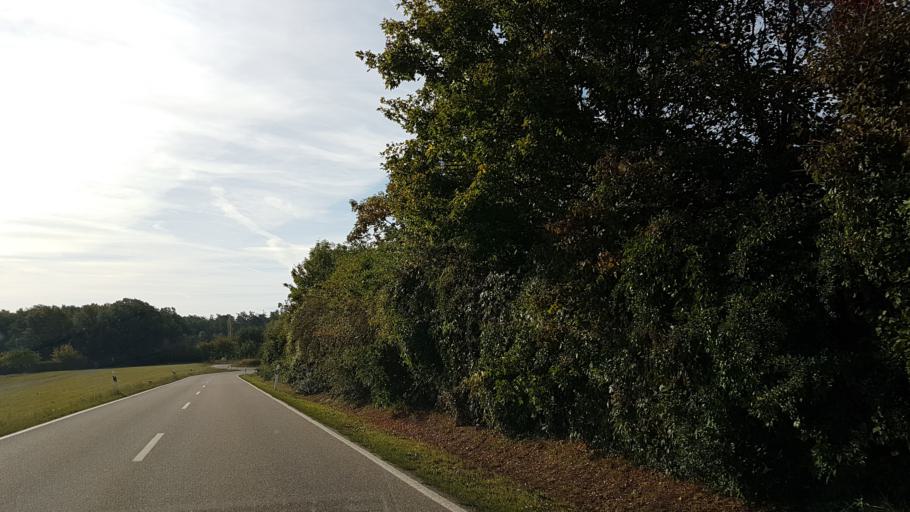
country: DE
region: Baden-Wuerttemberg
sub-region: Regierungsbezirk Stuttgart
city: Cleebronn
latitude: 49.0378
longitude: 9.0569
